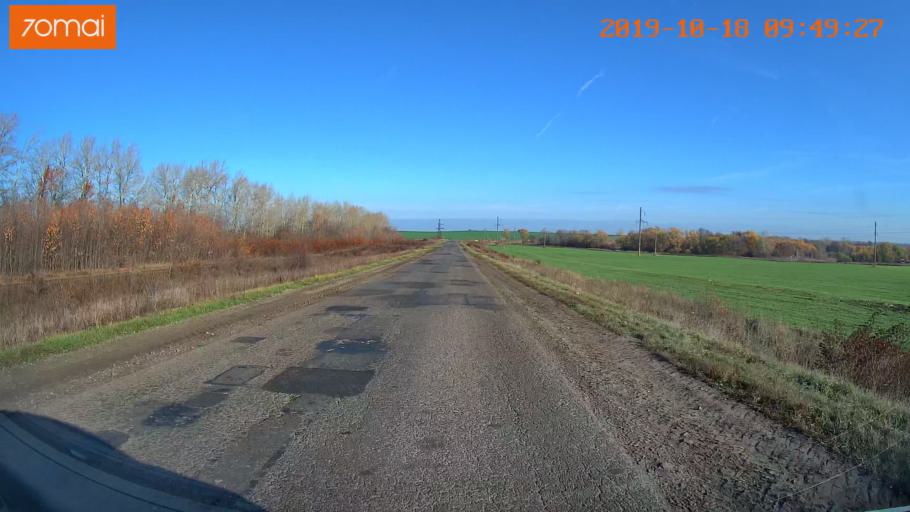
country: RU
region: Tula
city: Kazachka
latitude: 53.3181
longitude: 38.2680
